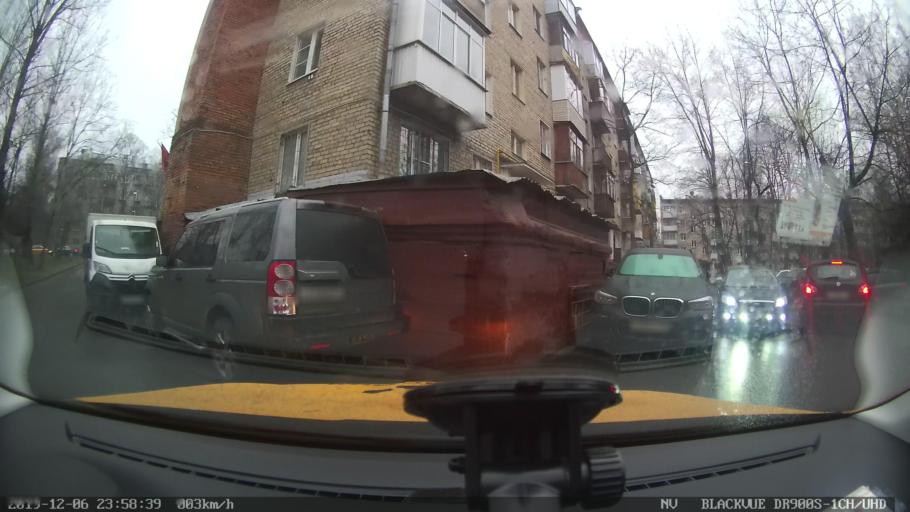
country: RU
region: Moscow
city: Leonovo
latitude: 55.8588
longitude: 37.6725
